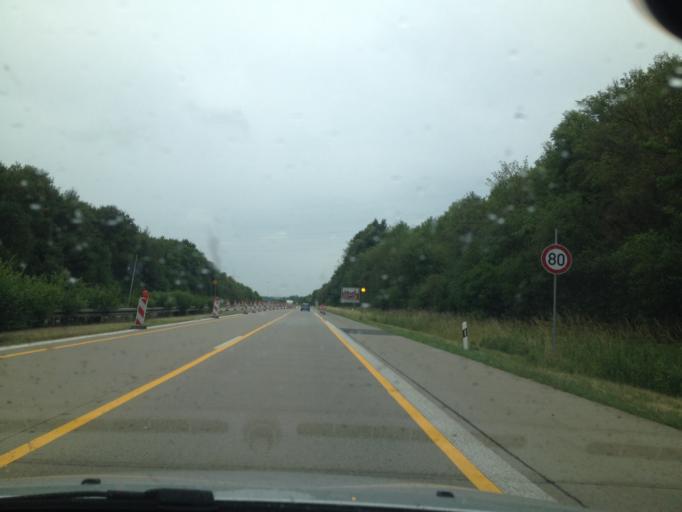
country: DE
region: Bavaria
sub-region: Regierungsbezirk Unterfranken
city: Biebelried
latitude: 49.7392
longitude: 10.1063
